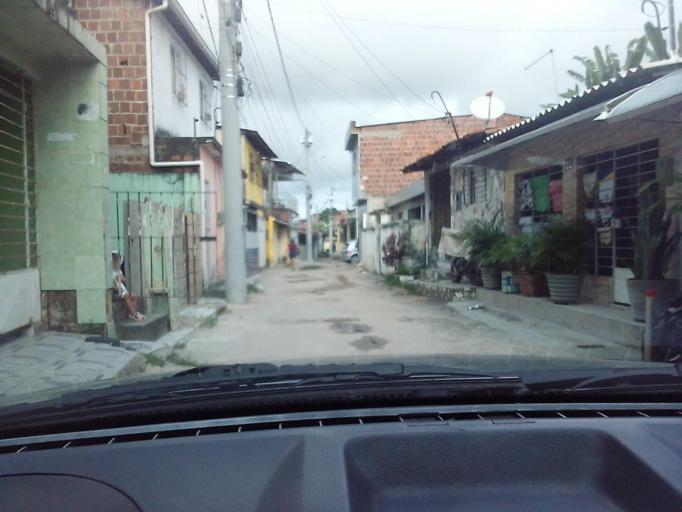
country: BR
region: Pernambuco
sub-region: Paulista
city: Paulista
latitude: -7.9460
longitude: -34.8994
